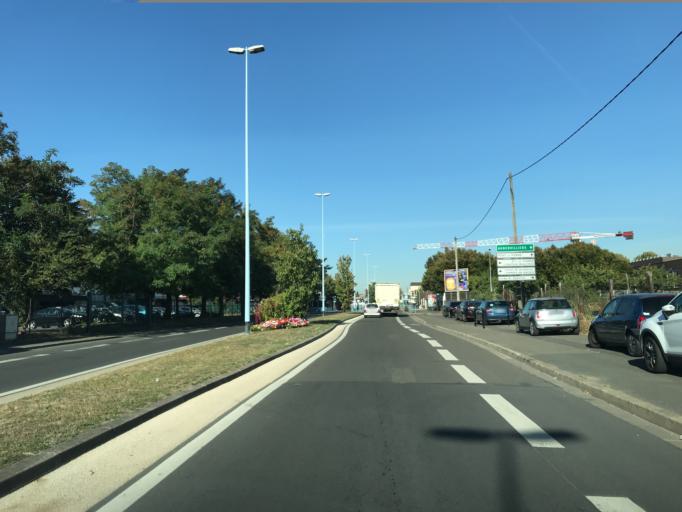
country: FR
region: Ile-de-France
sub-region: Departement de Seine-Saint-Denis
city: Bobigny
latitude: 48.9068
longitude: 2.4312
